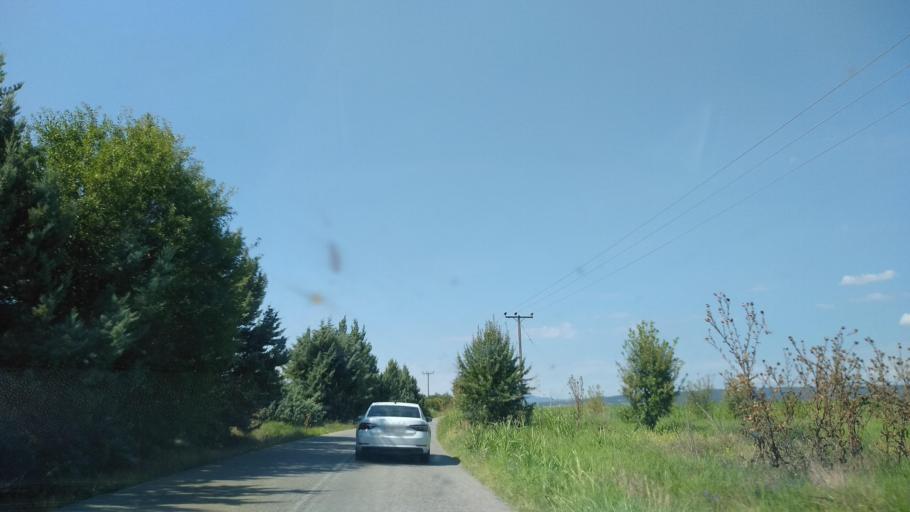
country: GR
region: Central Macedonia
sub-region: Nomos Thessalonikis
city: Nea Apollonia
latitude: 40.6299
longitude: 23.4751
